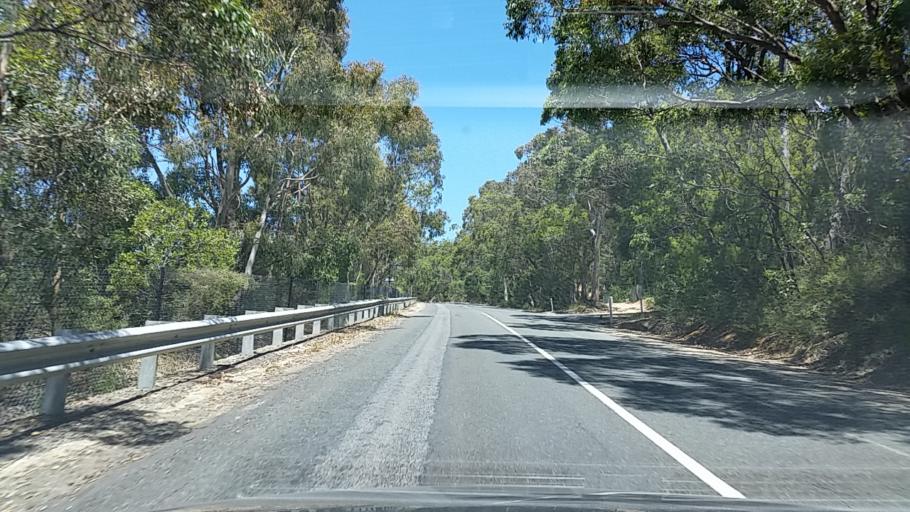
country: AU
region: South Australia
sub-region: Adelaide Hills
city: Crafers
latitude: -34.9911
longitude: 138.6946
